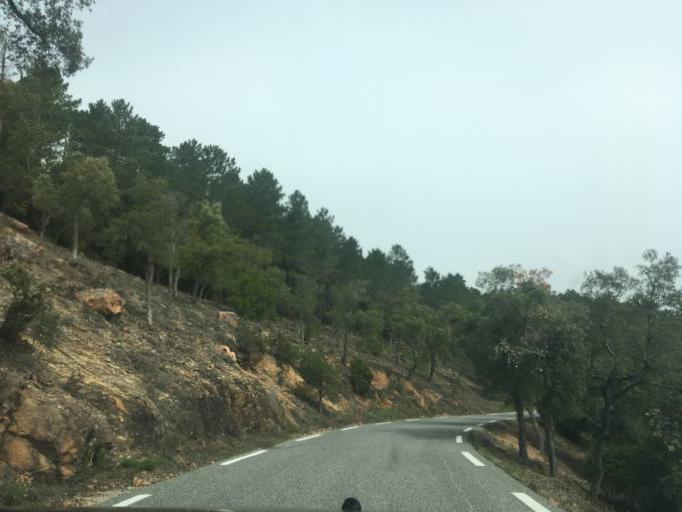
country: FR
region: Provence-Alpes-Cote d'Azur
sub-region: Departement du Var
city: Bagnols-en-Foret
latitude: 43.5162
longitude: 6.6472
